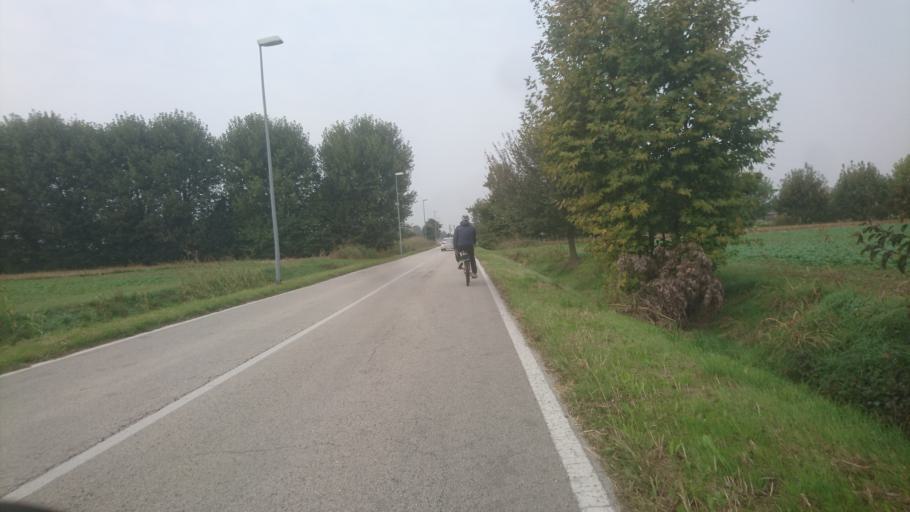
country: IT
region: Veneto
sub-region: Provincia di Vicenza
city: Camisano Vicentino
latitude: 45.5269
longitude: 11.7071
